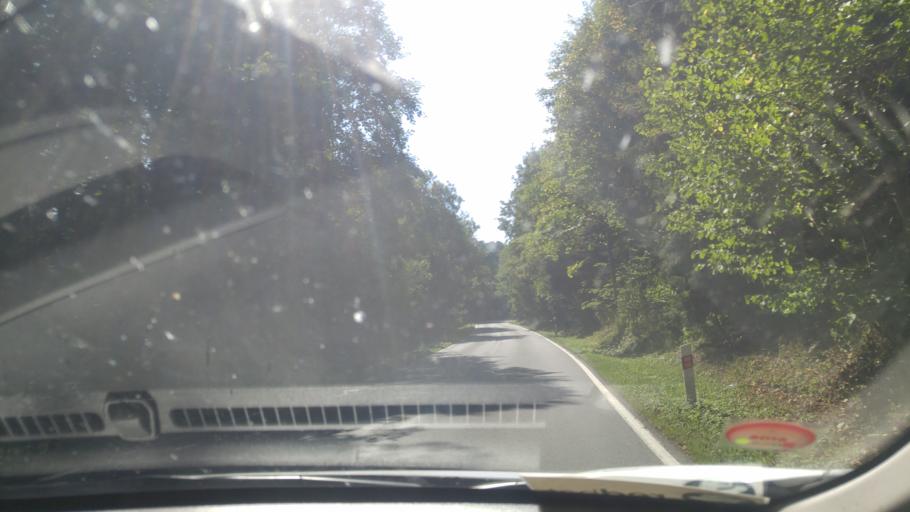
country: CZ
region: Olomoucky
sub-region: Okres Sumperk
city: Stare Mesto
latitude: 50.1651
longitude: 17.0274
